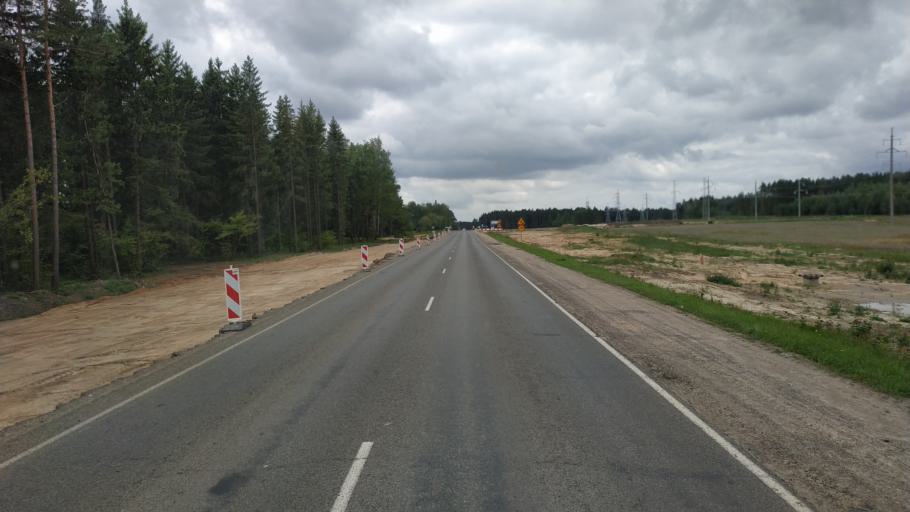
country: BY
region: Mogilev
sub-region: Mahilyowski Rayon
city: Veyno
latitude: 53.8744
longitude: 30.4371
